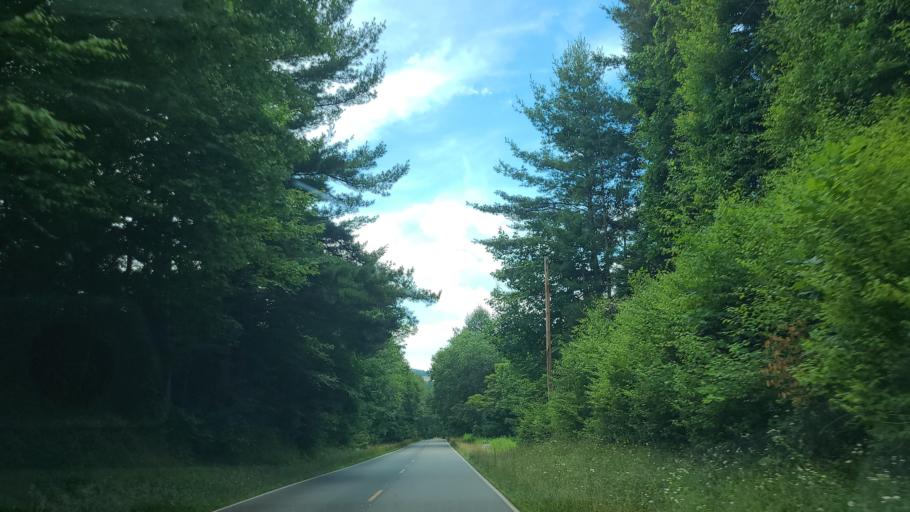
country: US
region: North Carolina
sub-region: Ashe County
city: Jefferson
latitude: 36.3934
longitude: -81.3389
